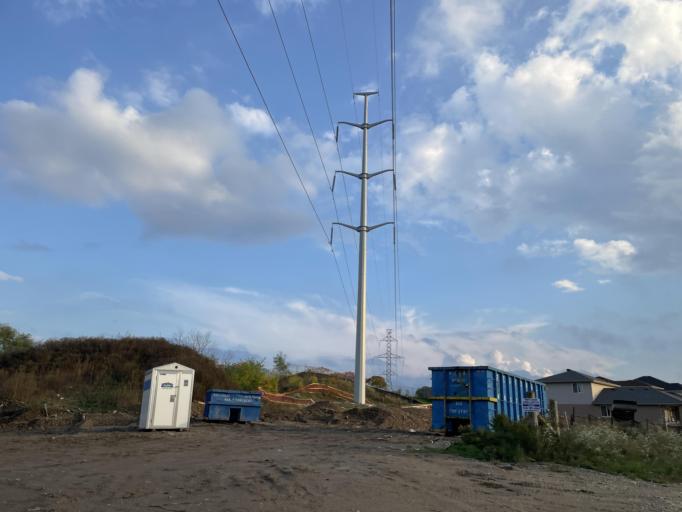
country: CA
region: Ontario
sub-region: Wellington County
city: Guelph
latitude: 43.5258
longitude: -80.2687
